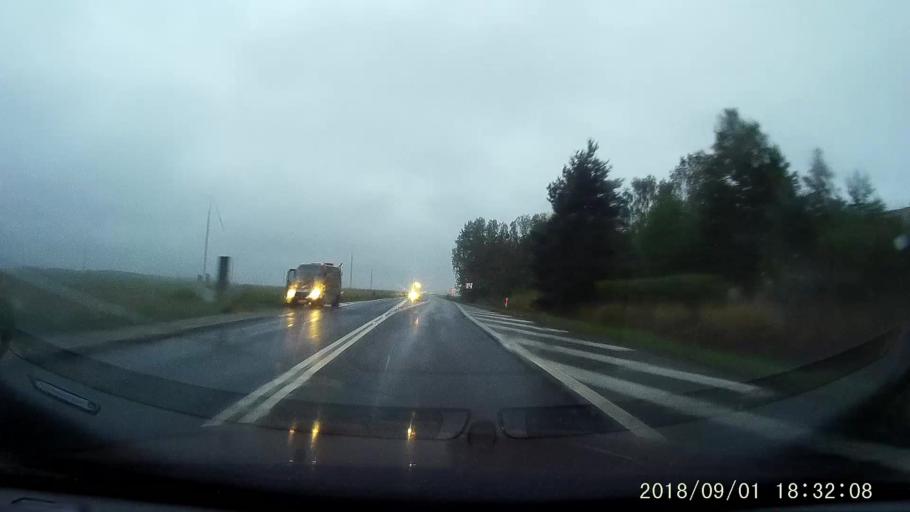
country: PL
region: Lower Silesian Voivodeship
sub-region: Powiat zgorzelecki
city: Lagow
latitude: 51.1941
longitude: 15.0812
